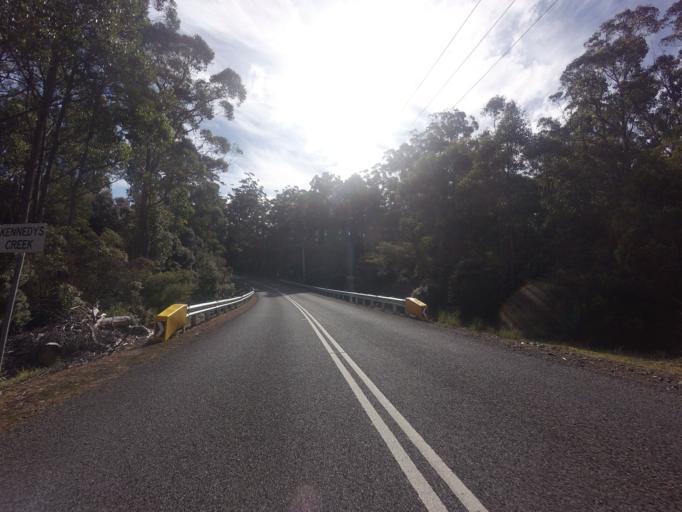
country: AU
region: Tasmania
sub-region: Clarence
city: Sandford
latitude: -43.1291
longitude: 147.7814
